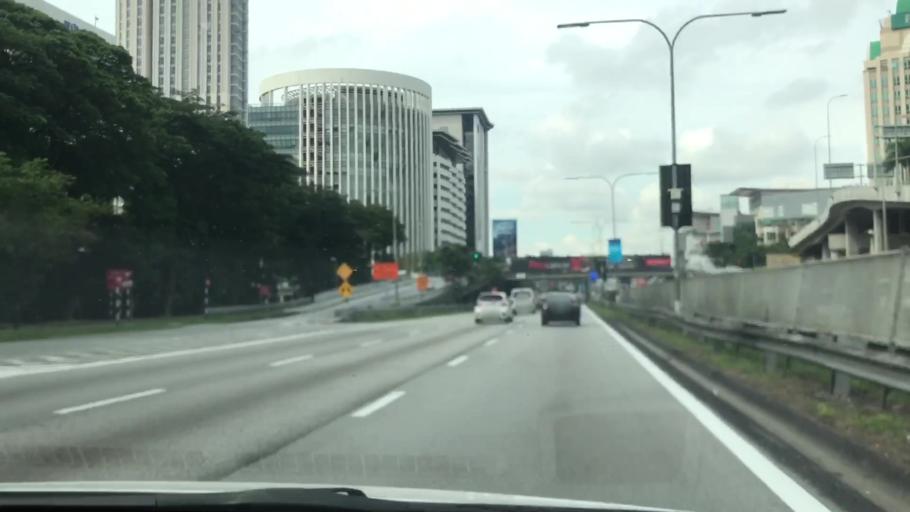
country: MY
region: Selangor
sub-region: Petaling
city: Petaling Jaya
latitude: 3.1036
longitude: 101.6413
